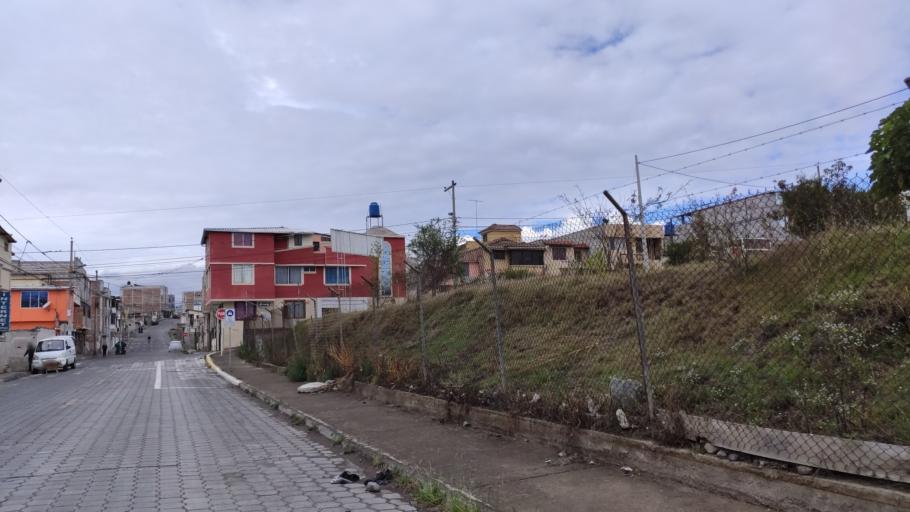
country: EC
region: Chimborazo
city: Riobamba
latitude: -1.6551
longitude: -78.6418
